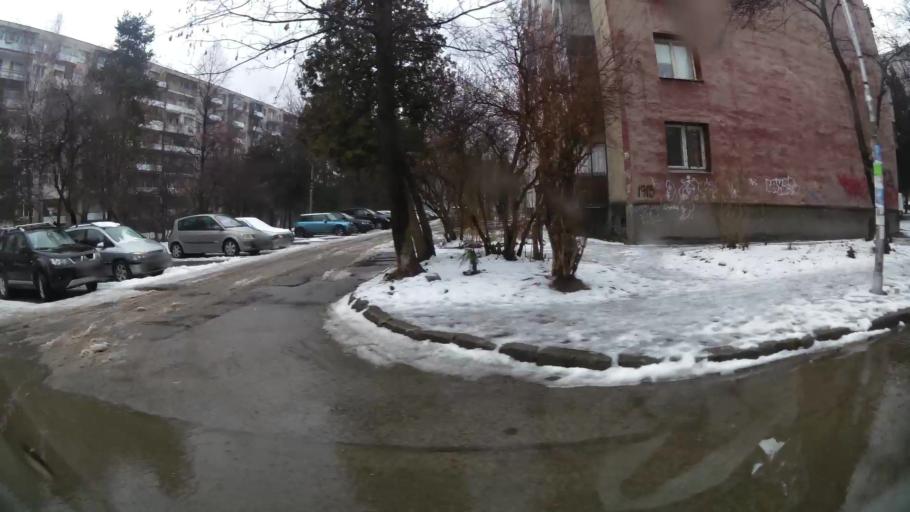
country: BG
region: Sofia-Capital
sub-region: Stolichna Obshtina
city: Sofia
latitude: 42.6670
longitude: 23.2723
